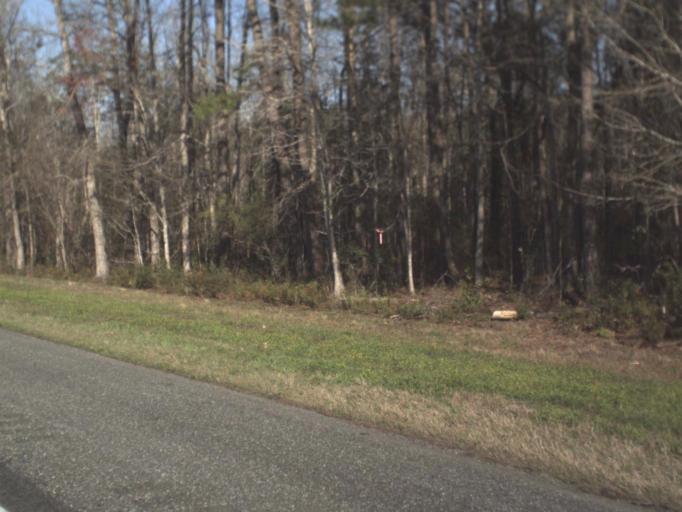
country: US
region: Florida
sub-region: Jefferson County
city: Monticello
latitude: 30.4728
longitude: -83.8309
